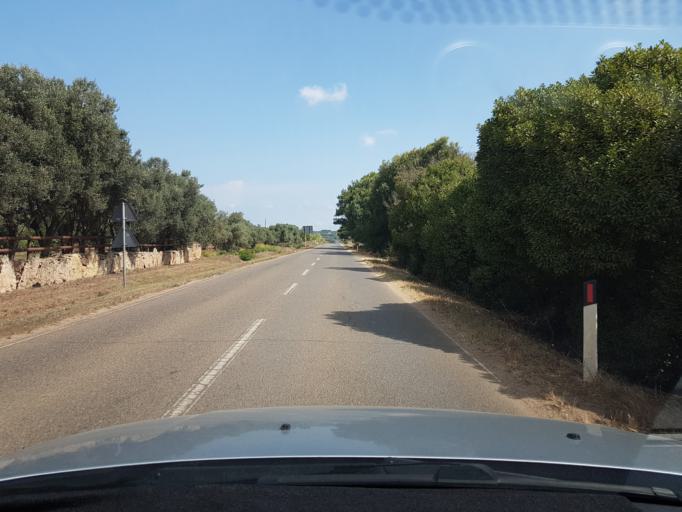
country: IT
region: Sardinia
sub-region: Provincia di Oristano
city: Cabras
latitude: 39.9029
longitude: 8.4364
